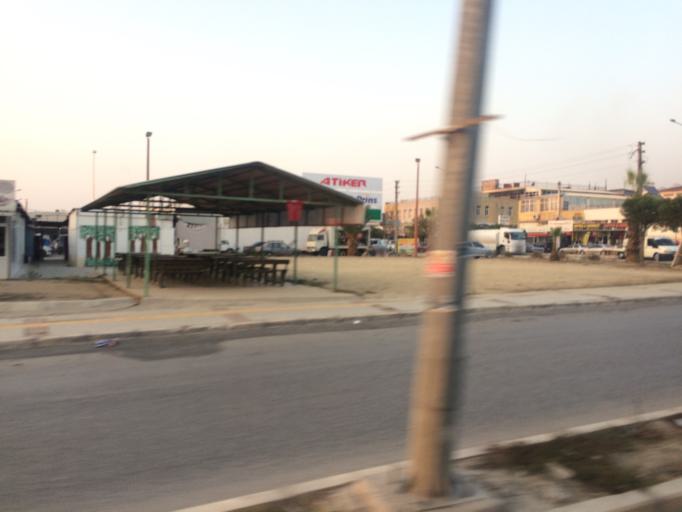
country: TR
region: Izmir
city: Karsiyaka
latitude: 38.4994
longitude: 27.0469
